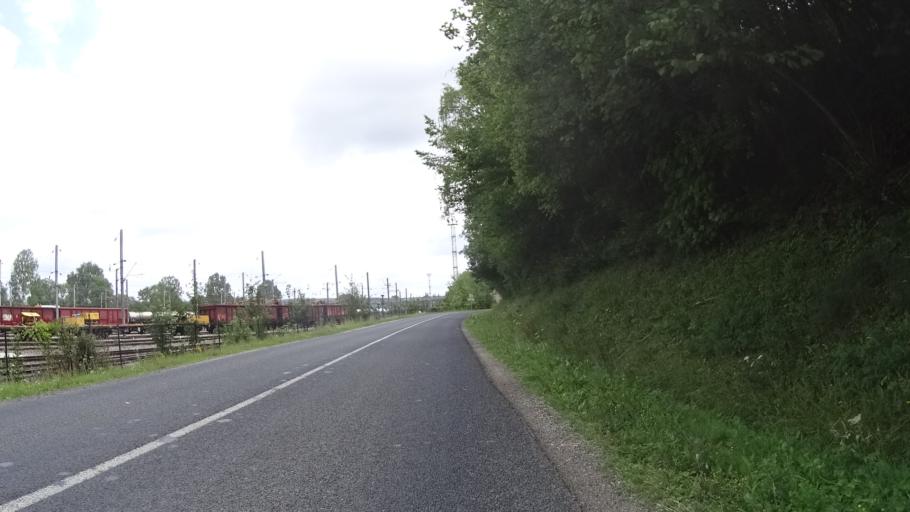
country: FR
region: Lorraine
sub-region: Departement de la Meuse
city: Lerouville
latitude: 48.7982
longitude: 5.5350
